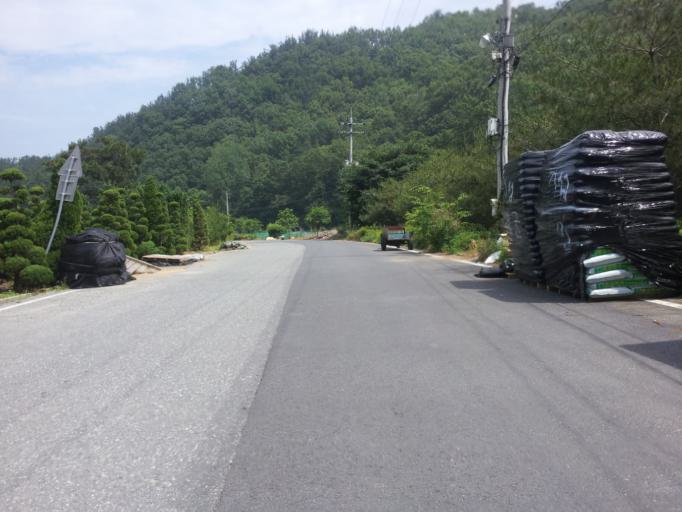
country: KR
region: Daejeon
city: Daejeon
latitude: 36.3328
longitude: 127.4929
